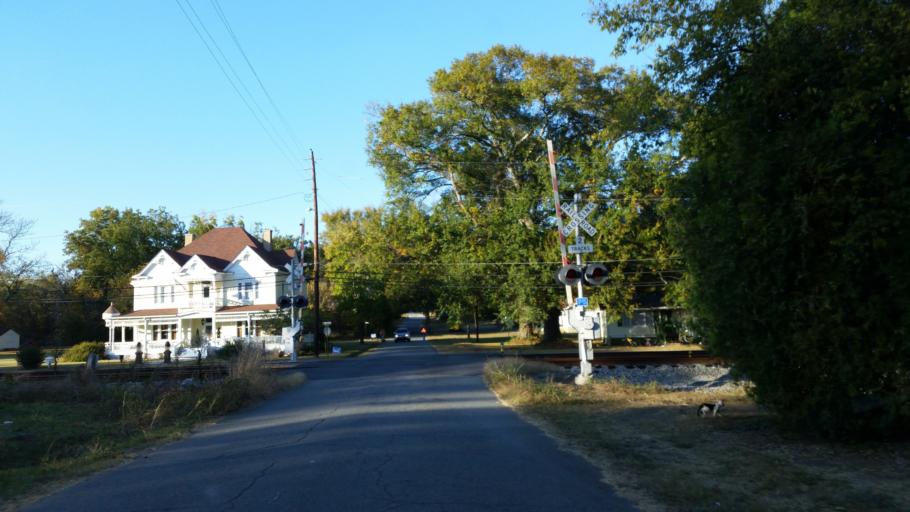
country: US
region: Georgia
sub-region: Bartow County
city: Euharlee
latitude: 34.2360
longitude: -84.9436
